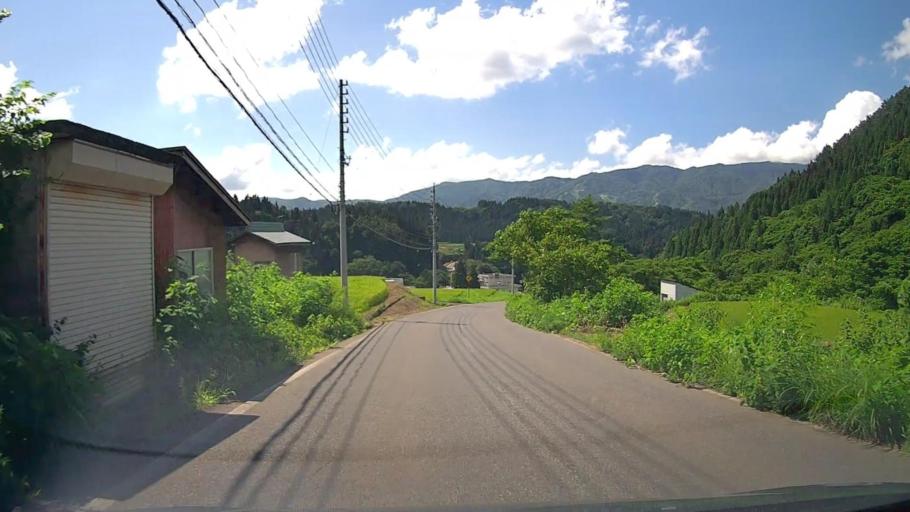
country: JP
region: Nagano
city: Iiyama
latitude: 36.9231
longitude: 138.4314
